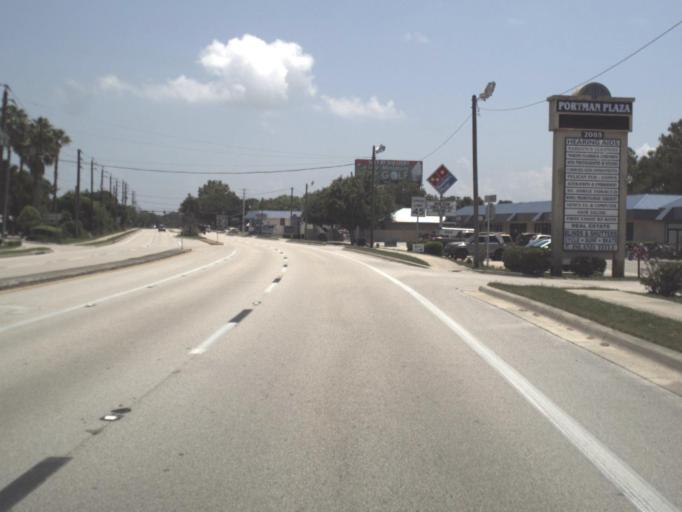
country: US
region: Florida
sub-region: Saint Johns County
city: Saint Augustine Beach
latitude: 29.8583
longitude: -81.2814
